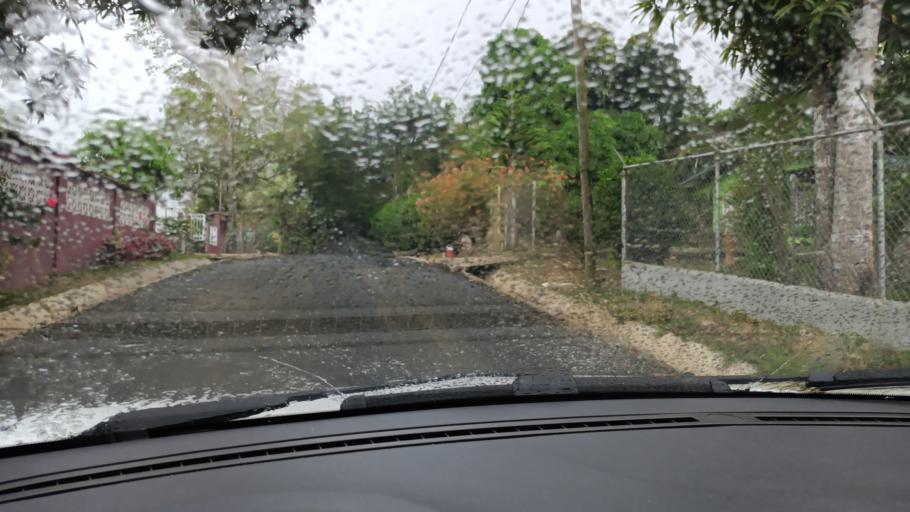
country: PA
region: Panama
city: Calzada Larga
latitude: 9.1646
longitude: -79.5510
